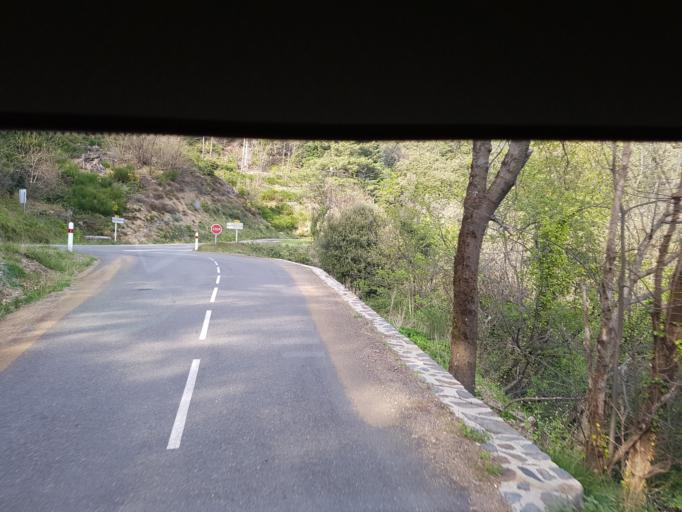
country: FR
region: Languedoc-Roussillon
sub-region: Departement du Gard
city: Branoux-les-Taillades
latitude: 44.3319
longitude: 3.9260
